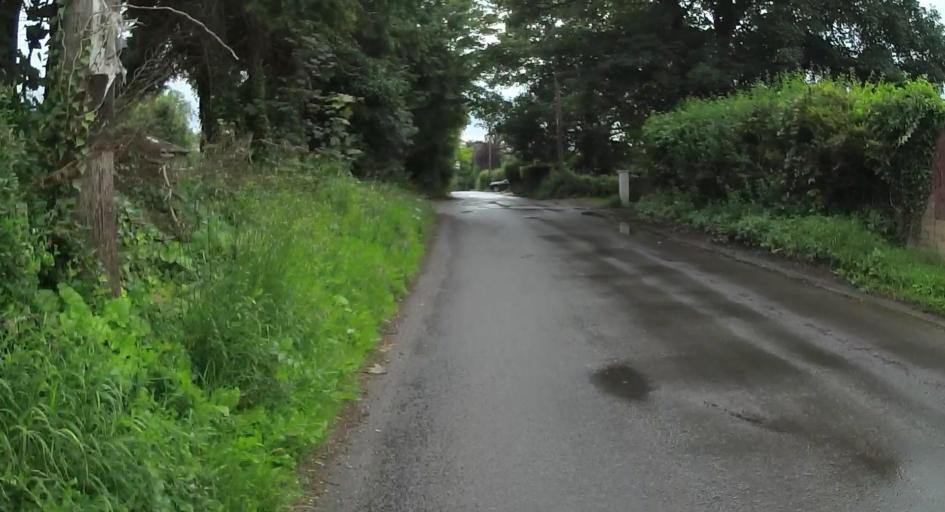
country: GB
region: England
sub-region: Hampshire
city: Andover
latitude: 51.2182
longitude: -1.4406
